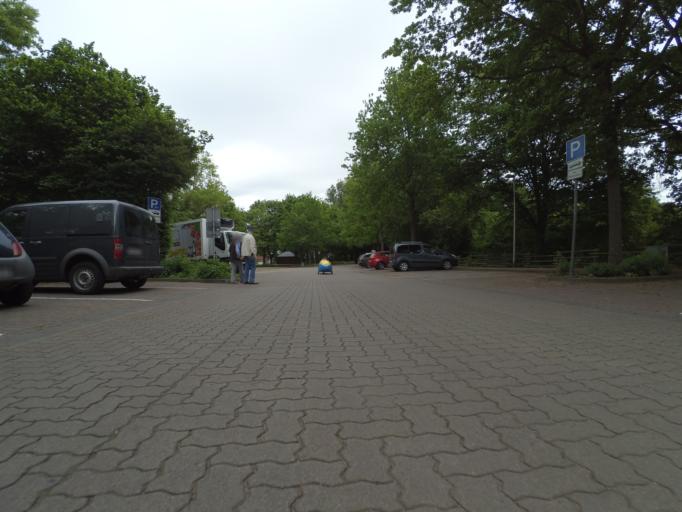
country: DE
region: Lower Saxony
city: Hagenburg
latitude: 52.4515
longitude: 9.3524
